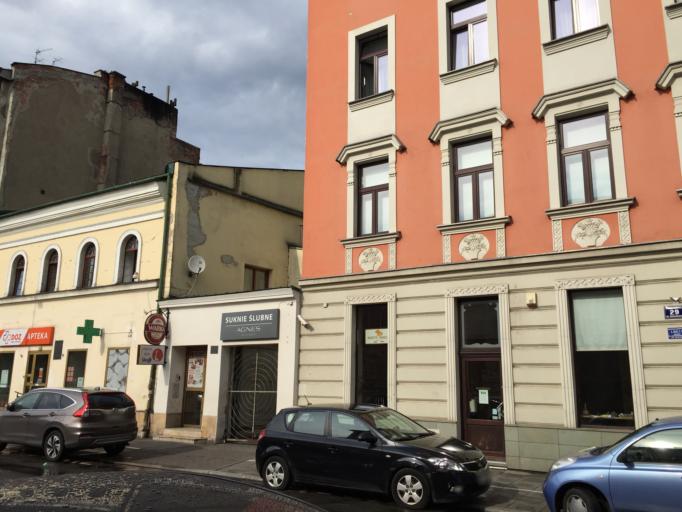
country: PL
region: Lesser Poland Voivodeship
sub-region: Krakow
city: Krakow
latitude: 50.0684
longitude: 19.9372
